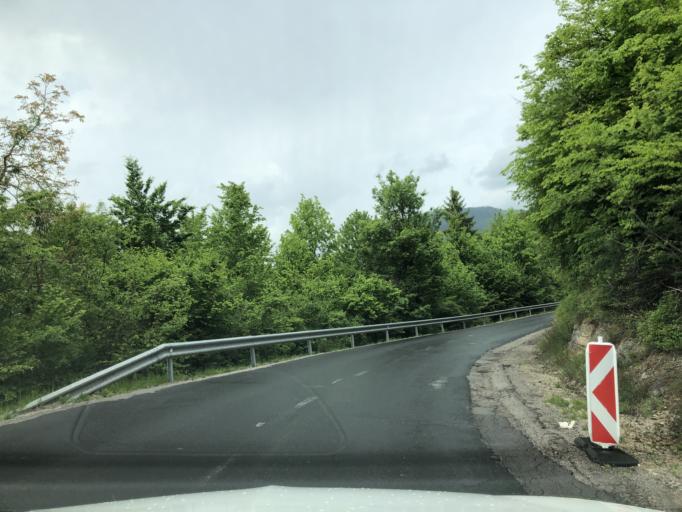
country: SI
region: Bloke
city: Nova Vas
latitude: 45.7627
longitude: 14.4324
